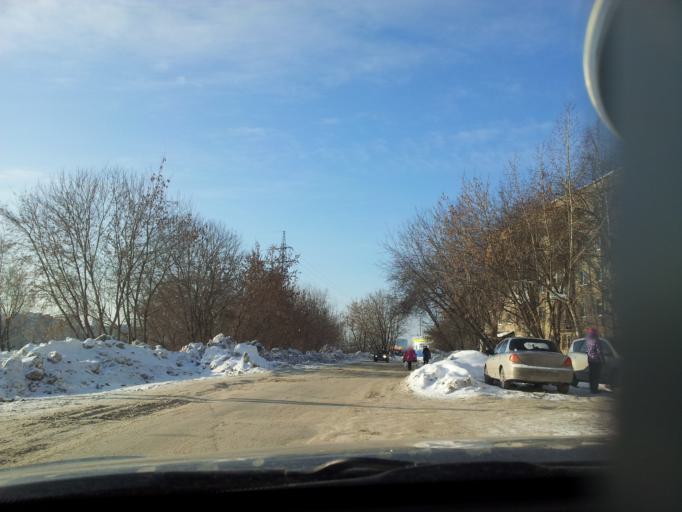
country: RU
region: Perm
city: Perm
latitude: 58.0207
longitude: 56.2701
